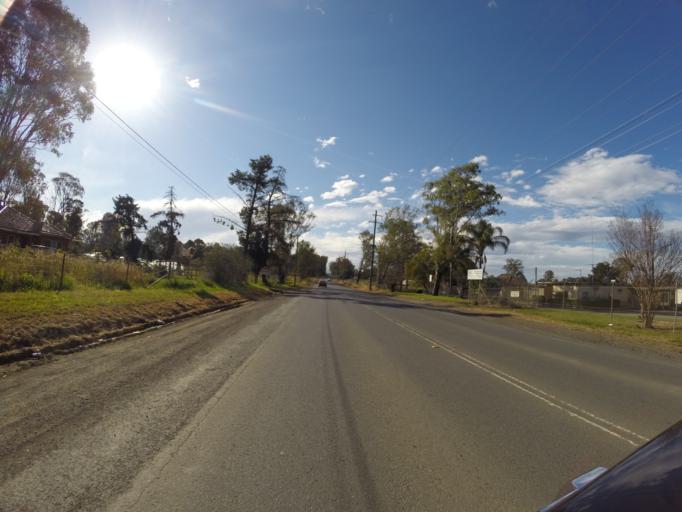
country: AU
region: New South Wales
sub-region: Liverpool
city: Bringelly
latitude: -33.9123
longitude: 150.7866
